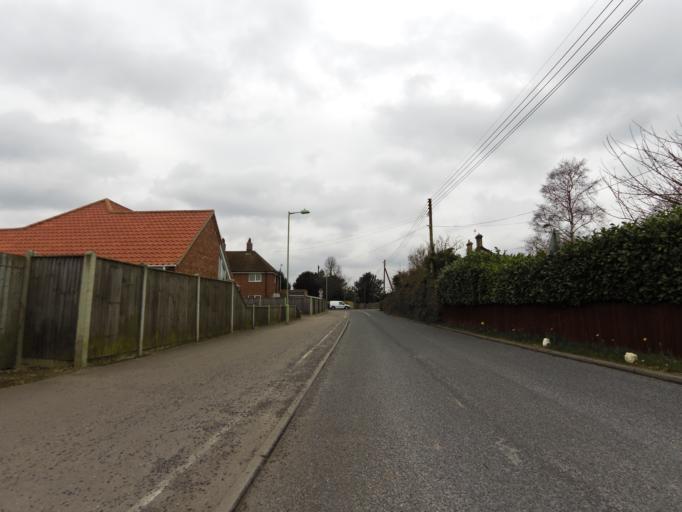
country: GB
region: England
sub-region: Suffolk
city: Halesworth
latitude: 52.3505
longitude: 1.5098
